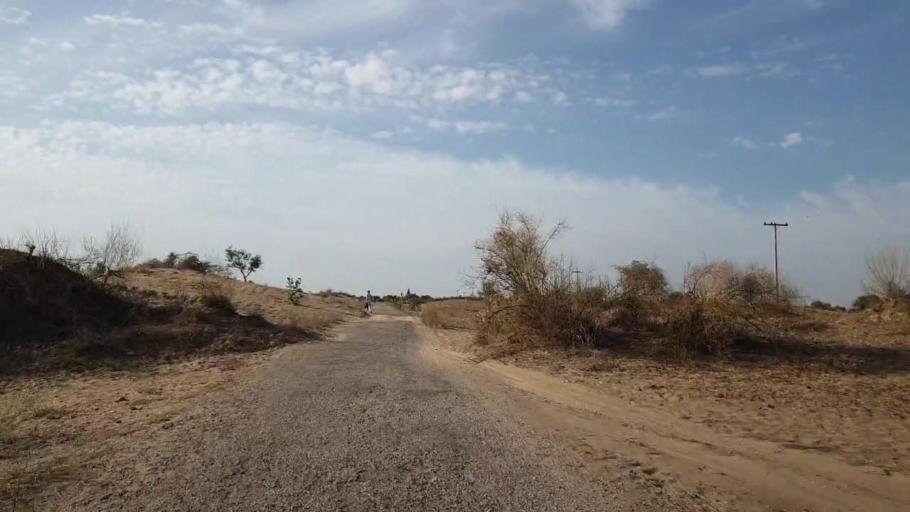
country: PK
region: Sindh
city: Nabisar
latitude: 25.0503
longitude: 69.9698
